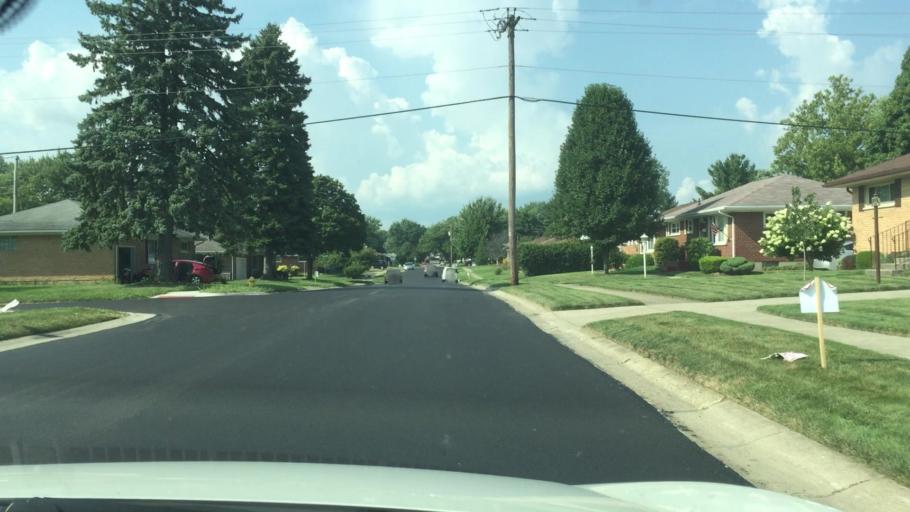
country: US
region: Ohio
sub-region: Clark County
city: Northridge
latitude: 39.9890
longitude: -83.7785
